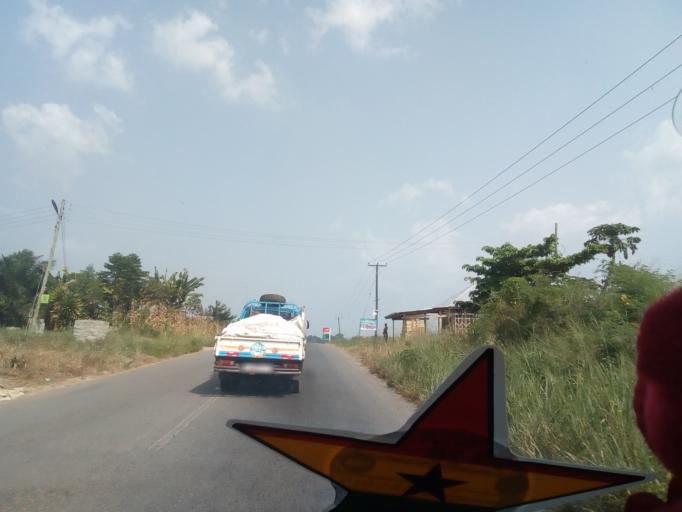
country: GH
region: Eastern
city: Suhum
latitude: 6.0446
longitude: -0.4192
